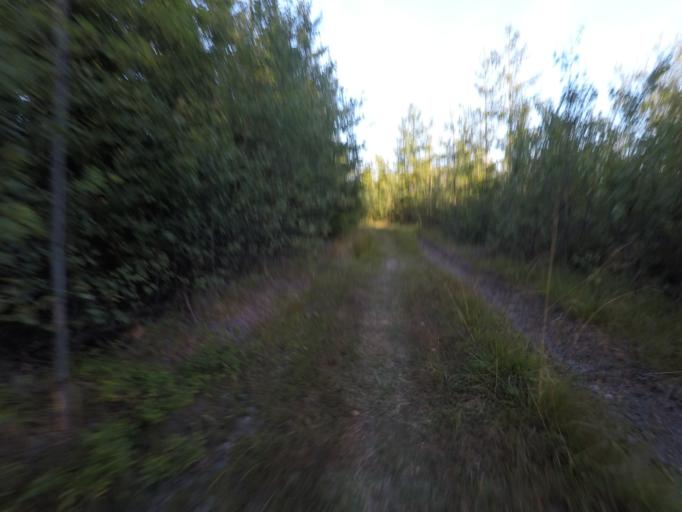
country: SE
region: Soedermanland
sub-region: Eskilstuna Kommun
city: Kvicksund
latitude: 59.4161
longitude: 16.3246
